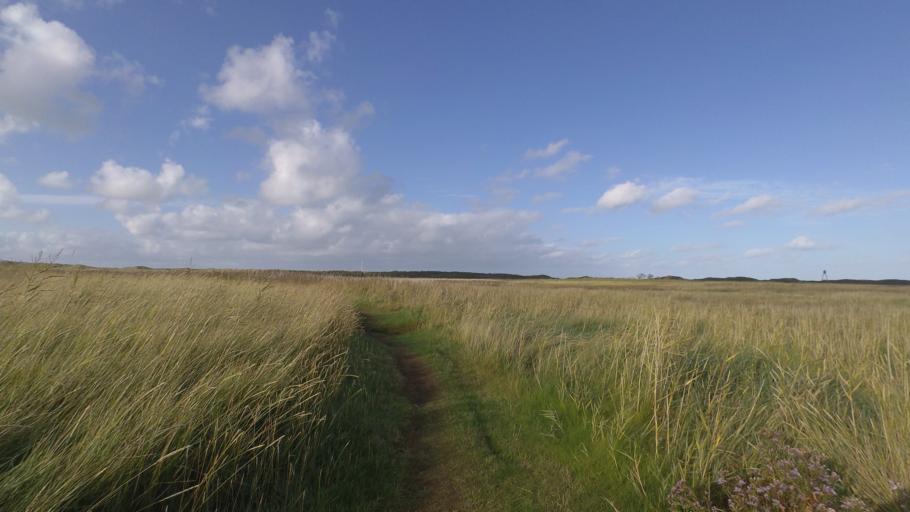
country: NL
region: Friesland
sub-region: Gemeente Dongeradeel
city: Ternaard
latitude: 53.4601
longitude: 5.9201
